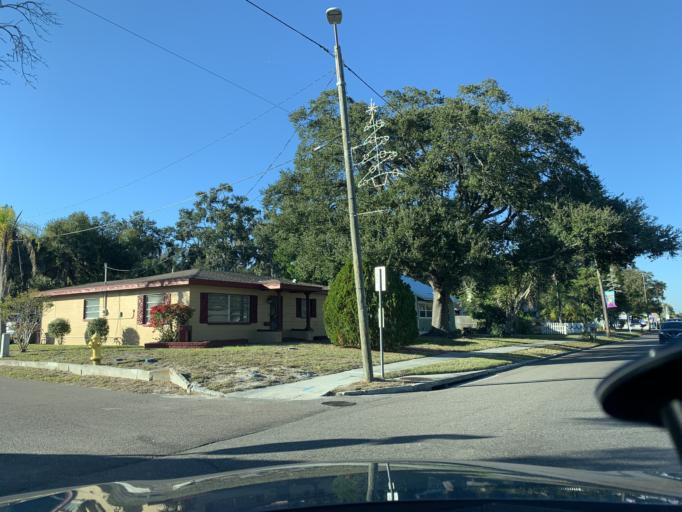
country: US
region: Florida
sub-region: Pinellas County
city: Gulfport
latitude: 27.7457
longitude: -82.6997
